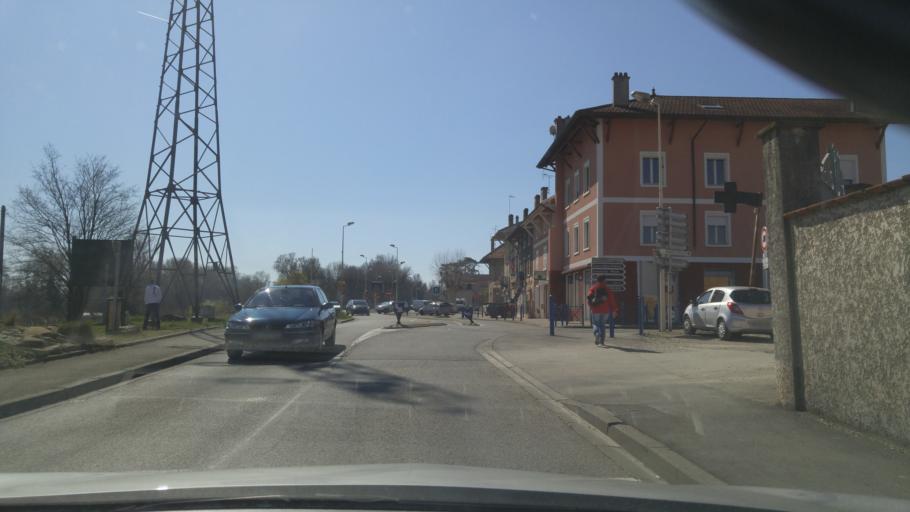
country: FR
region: Rhone-Alpes
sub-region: Departement de l'Isere
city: Tignieu-Jameyzieu
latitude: 45.7469
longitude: 5.1677
